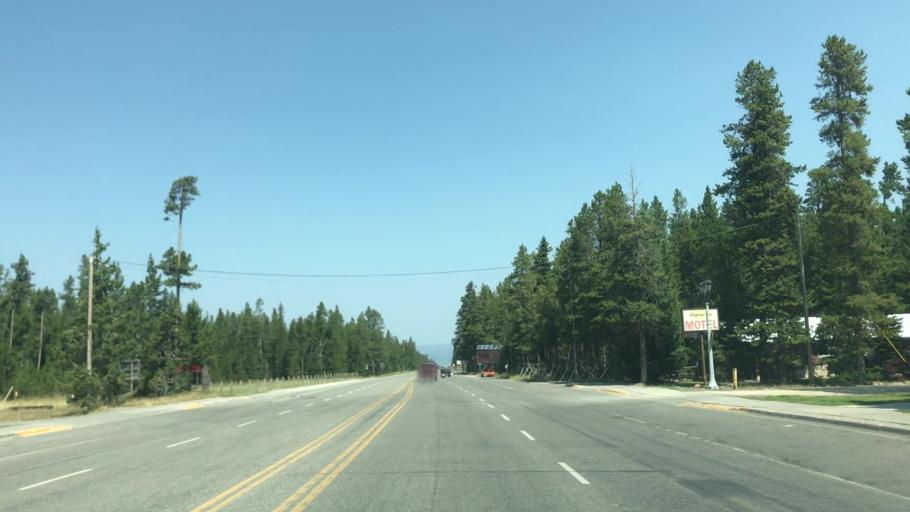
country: US
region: Montana
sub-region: Gallatin County
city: West Yellowstone
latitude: 44.6644
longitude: -111.0998
